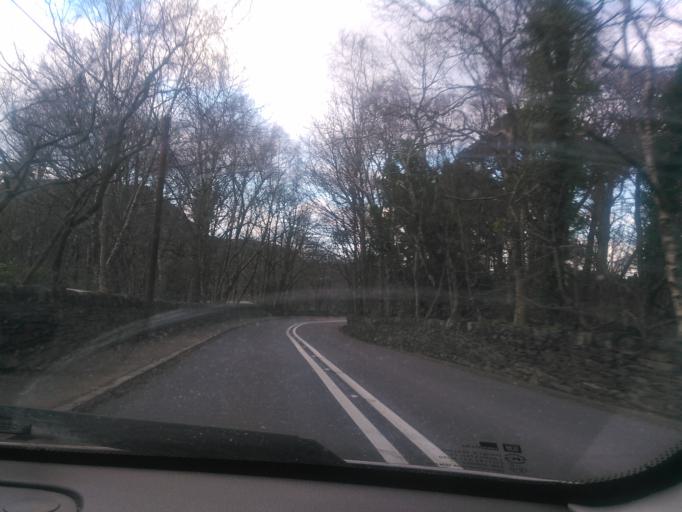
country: GB
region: Wales
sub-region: Gwynedd
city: Bethesda
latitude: 53.1698
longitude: -4.0564
